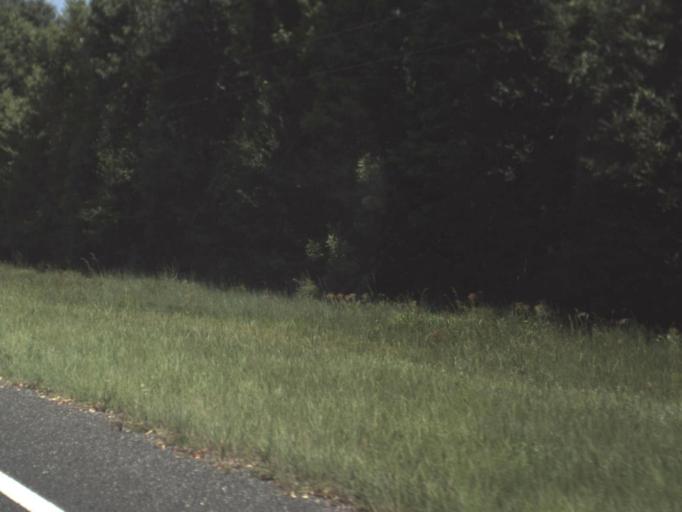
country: US
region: Florida
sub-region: Dixie County
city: Cross City
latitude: 29.6575
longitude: -83.1870
